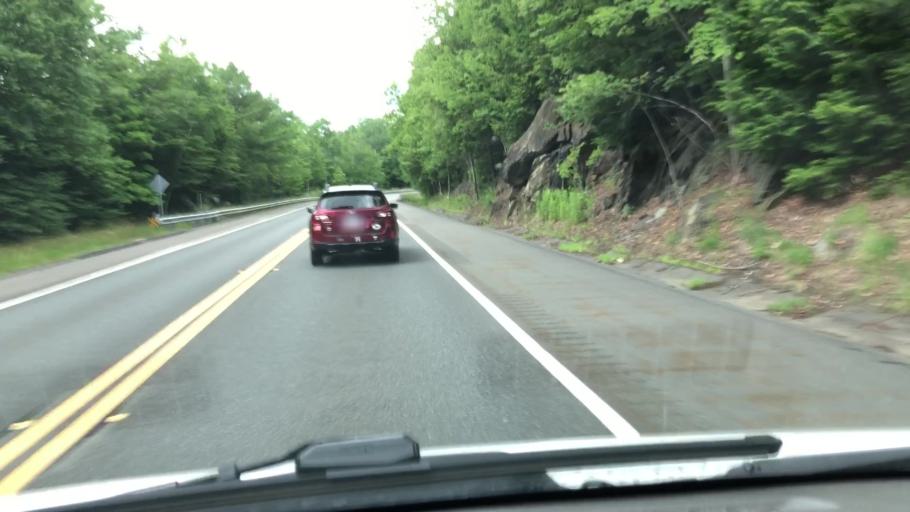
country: US
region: Massachusetts
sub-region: Hampshire County
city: Chesterfield
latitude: 42.4516
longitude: -72.8555
